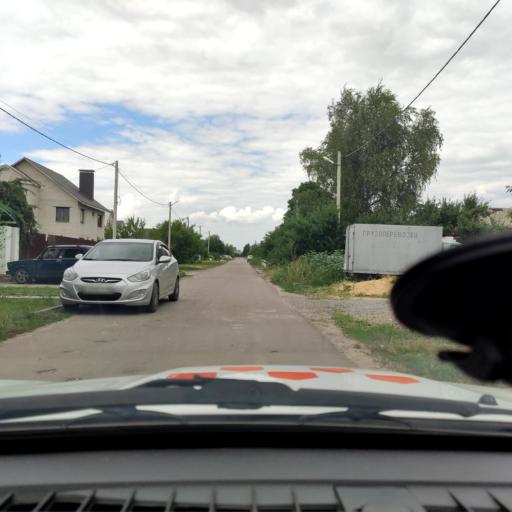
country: RU
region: Voronezj
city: Ramon'
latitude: 51.8285
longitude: 39.2590
